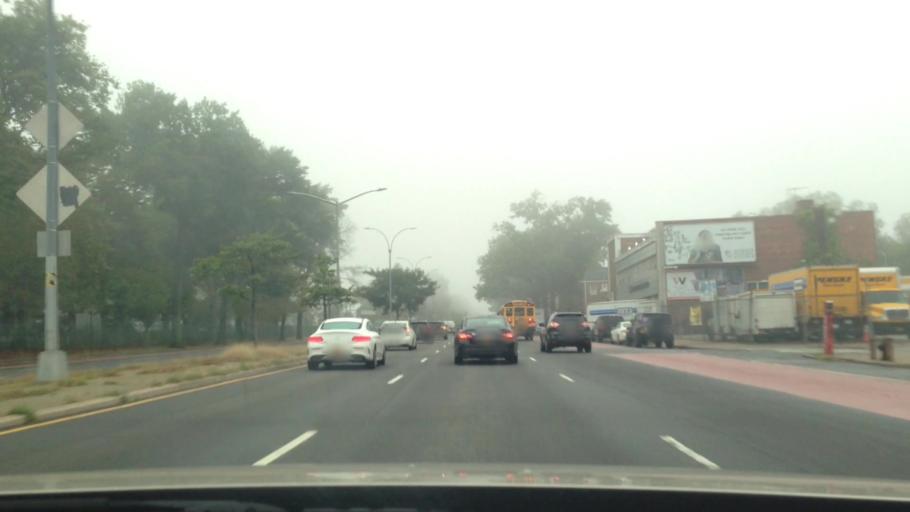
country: US
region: New York
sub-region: Queens County
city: Borough of Queens
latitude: 40.7153
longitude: -73.8603
